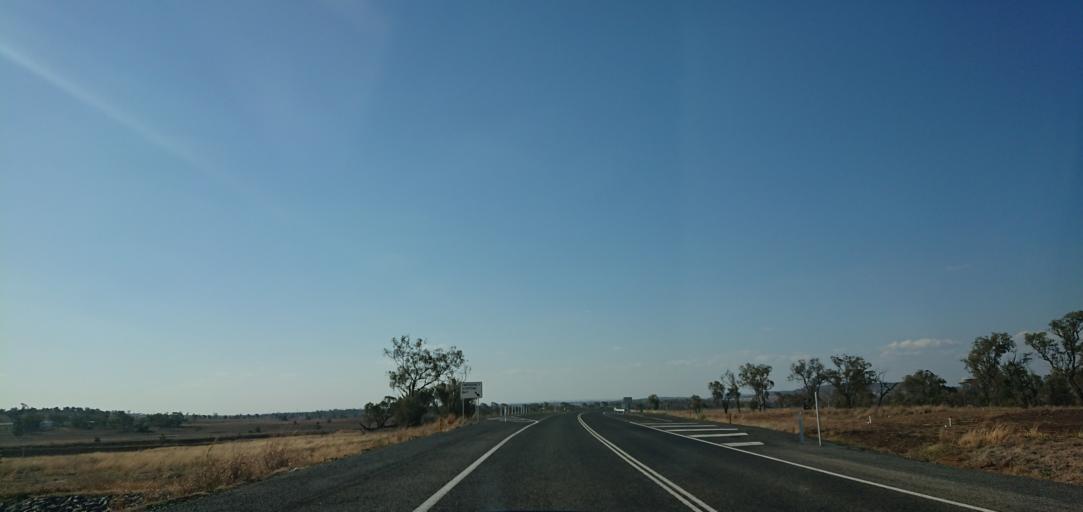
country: AU
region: Queensland
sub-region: Toowoomba
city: Westbrook
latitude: -27.6062
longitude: 151.7862
